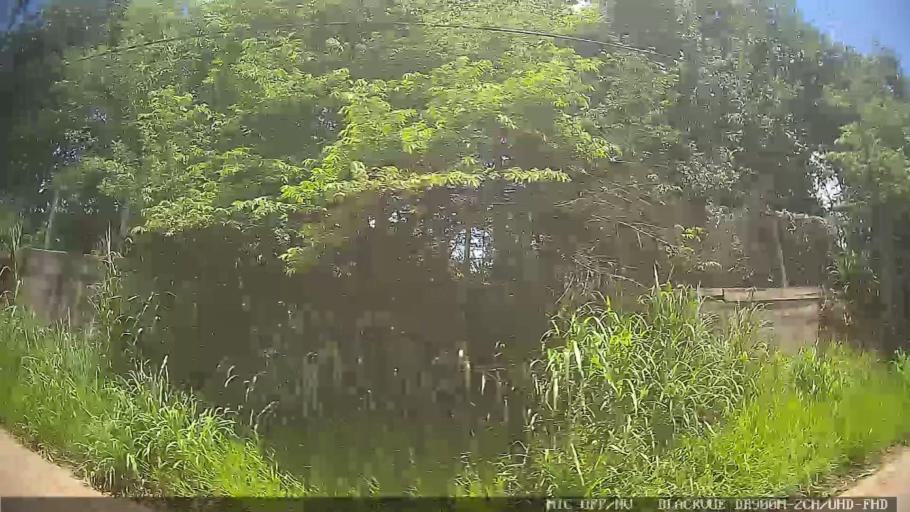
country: BR
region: Sao Paulo
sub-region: Braganca Paulista
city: Braganca Paulista
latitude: -22.9029
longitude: -46.5832
